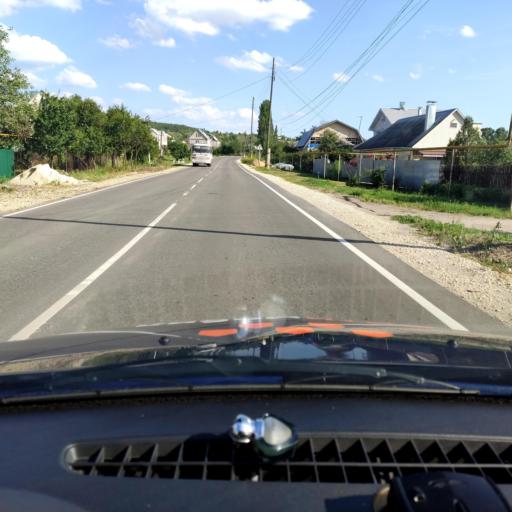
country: RU
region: Voronezj
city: Devitsa
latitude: 51.6551
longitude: 38.9706
